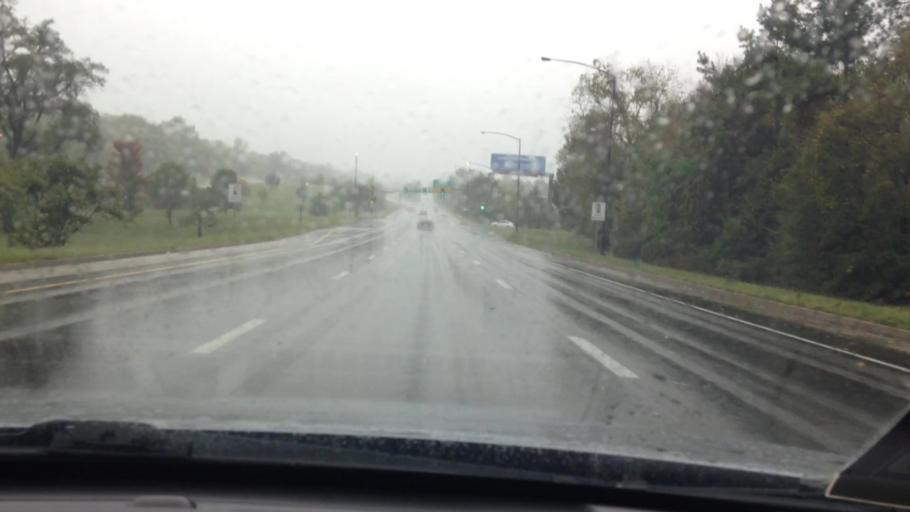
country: US
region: Kansas
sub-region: Johnson County
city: Mission Hills
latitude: 39.0209
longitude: -94.5547
